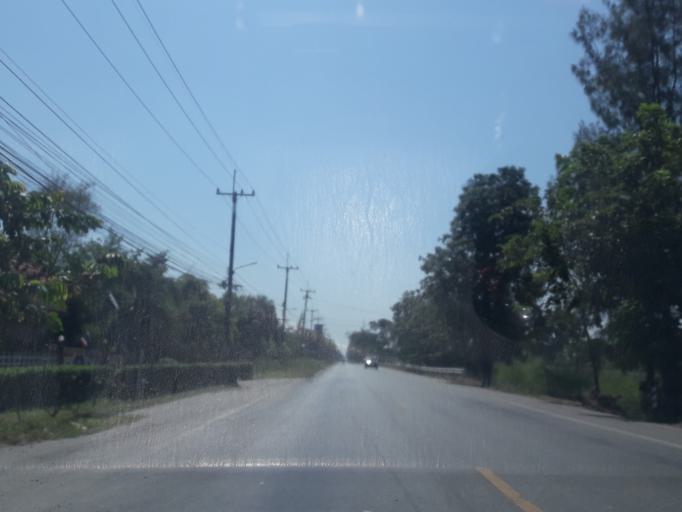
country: TH
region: Pathum Thani
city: Nong Suea
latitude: 14.1599
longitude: 100.8237
